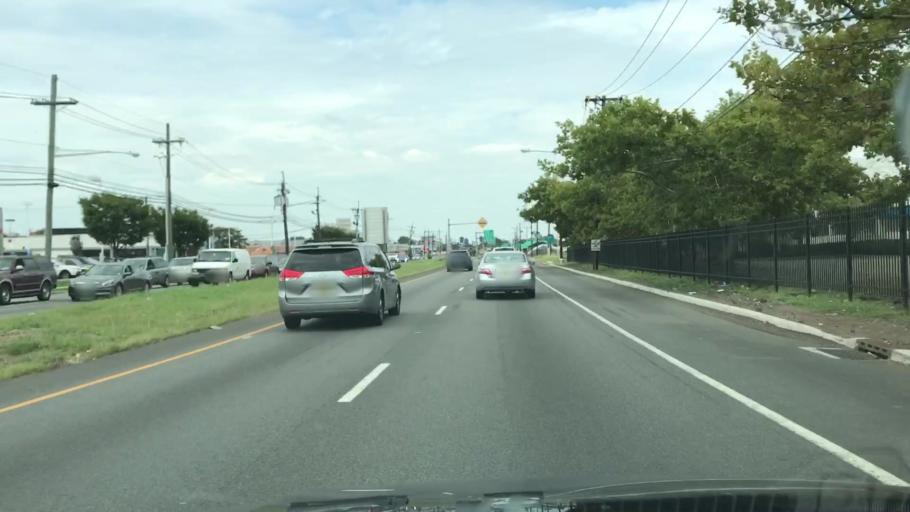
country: US
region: New Jersey
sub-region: Hudson County
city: Jersey City
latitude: 40.7167
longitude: -74.0952
